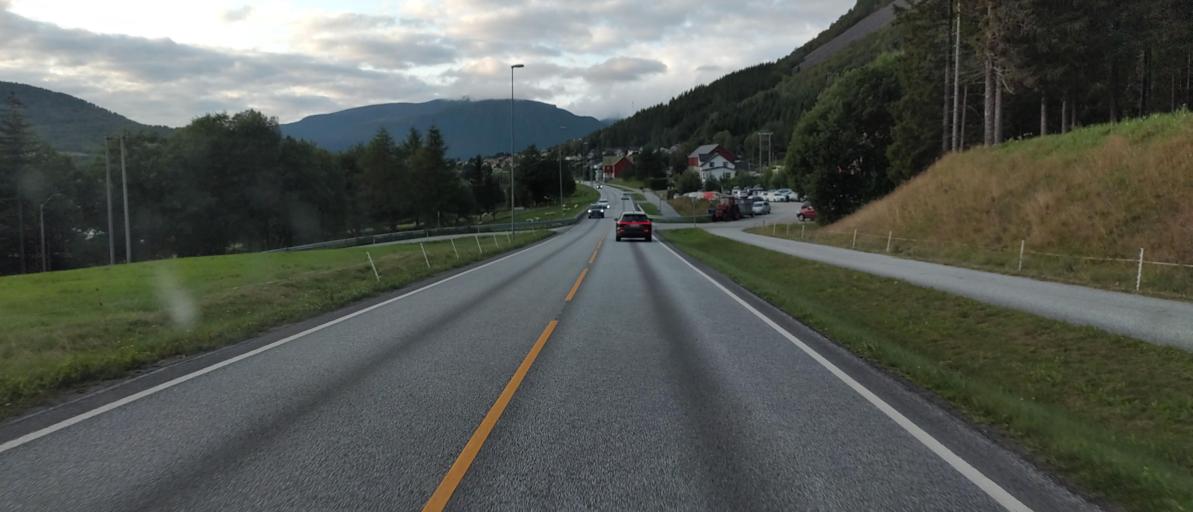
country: NO
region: More og Romsdal
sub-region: Molde
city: Molde
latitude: 62.8058
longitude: 7.2468
